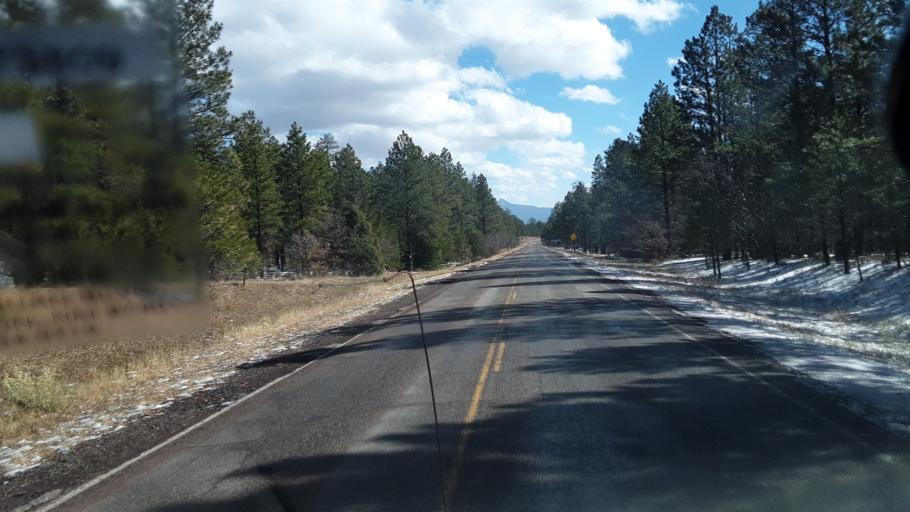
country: US
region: New Mexico
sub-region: Rio Arriba County
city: Santa Teresa
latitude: 36.1996
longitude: -106.7567
